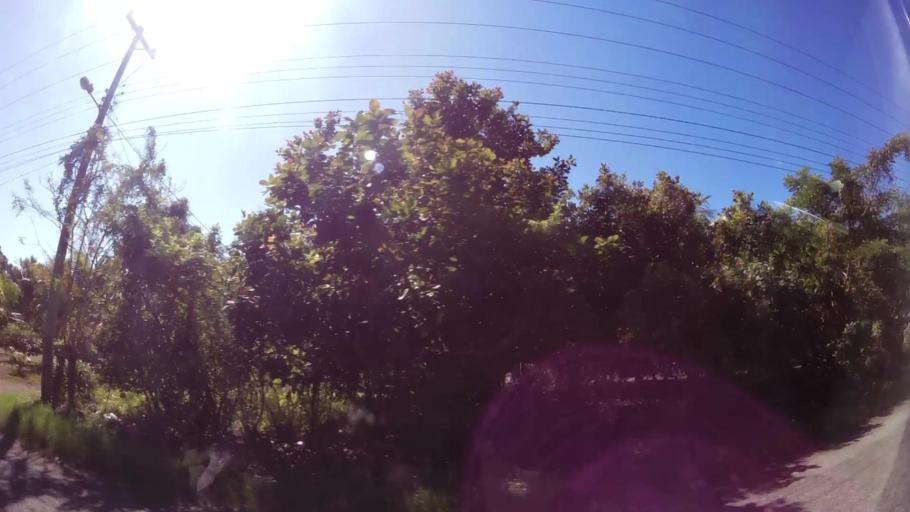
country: GT
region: Escuintla
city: Iztapa
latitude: 13.9243
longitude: -90.5821
